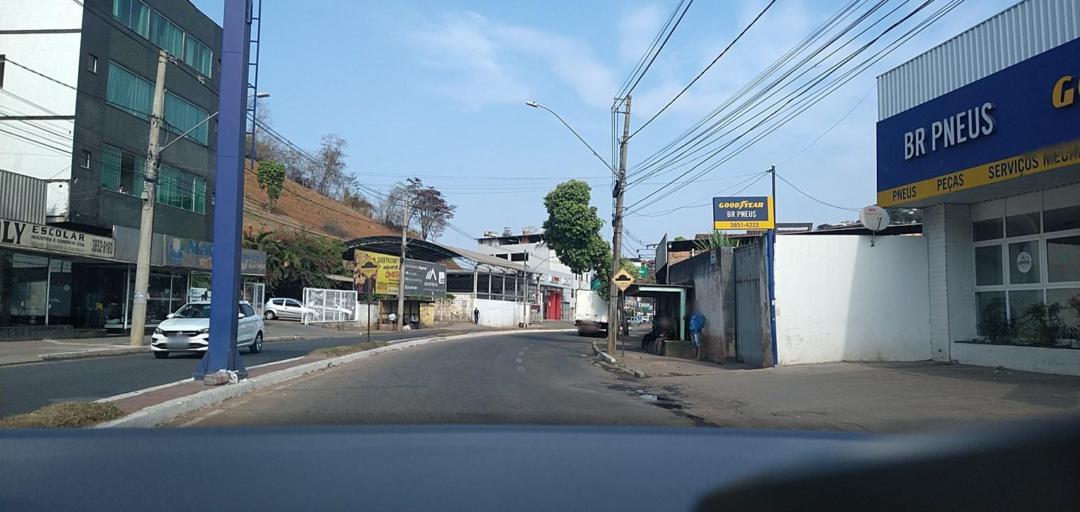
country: BR
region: Minas Gerais
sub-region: Joao Monlevade
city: Joao Monlevade
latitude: -19.8091
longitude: -43.1690
